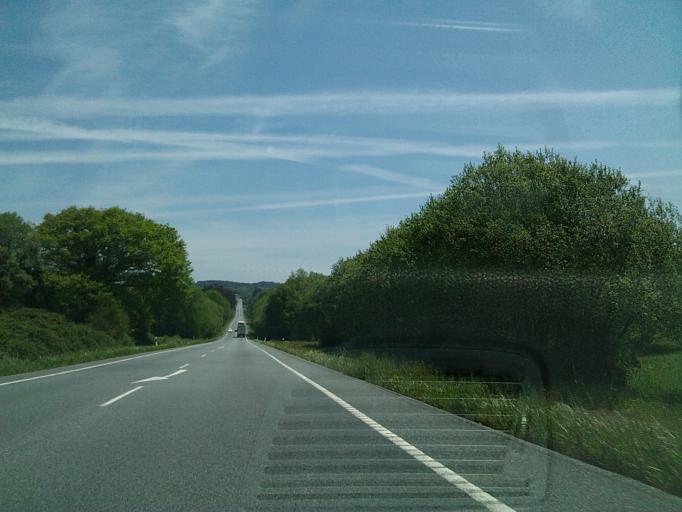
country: ES
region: Galicia
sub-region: Provincia da Coruna
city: Vilasantar
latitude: 43.1138
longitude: -8.1216
